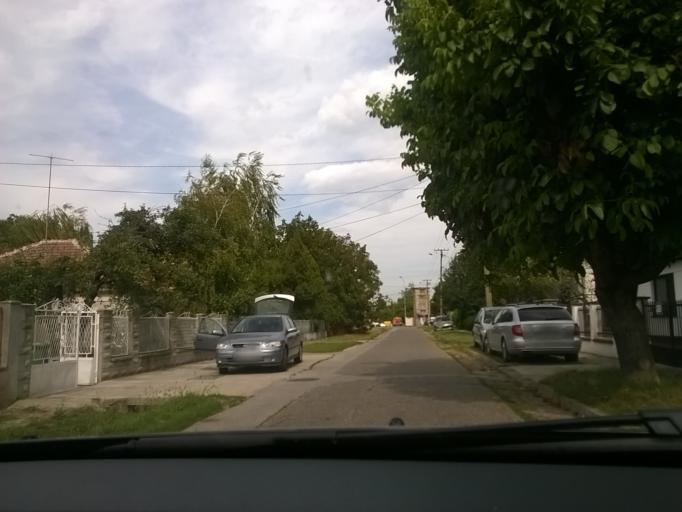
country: RS
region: Autonomna Pokrajina Vojvodina
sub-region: Juznobanatski Okrug
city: Vrsac
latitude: 45.1213
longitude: 21.2822
